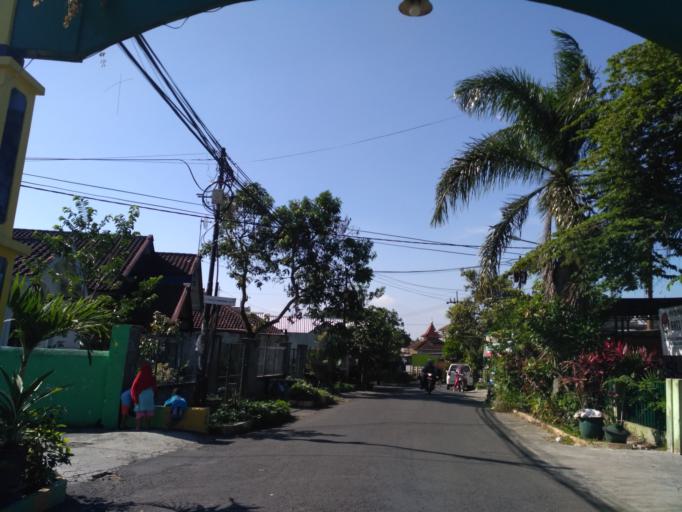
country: ID
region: East Java
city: Singosari
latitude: -7.9310
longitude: 112.6569
